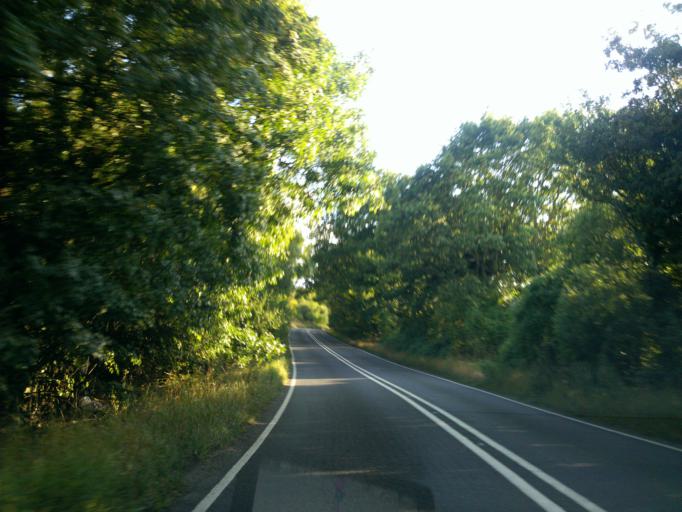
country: GB
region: England
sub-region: Essex
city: Sible Hedingham
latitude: 51.9580
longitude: 0.5975
